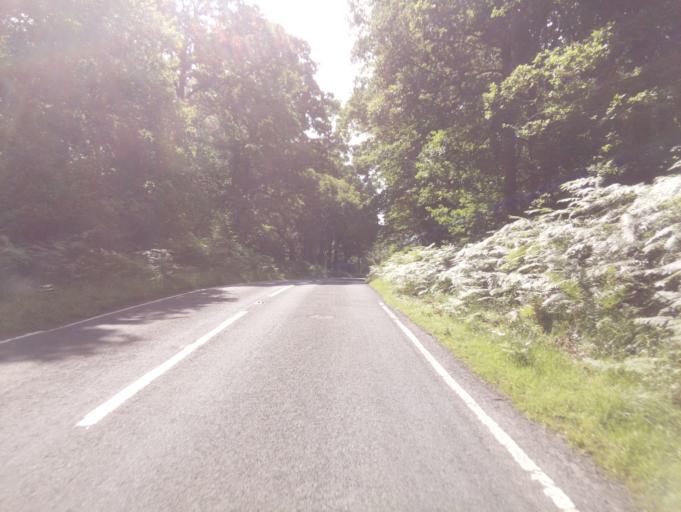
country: GB
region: England
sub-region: Gloucestershire
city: Cinderford
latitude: 51.7765
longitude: -2.5077
